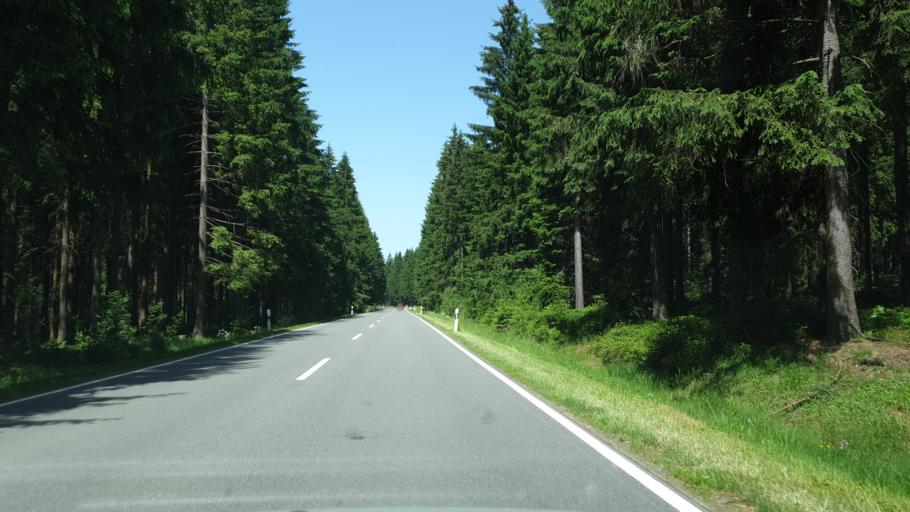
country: DE
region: Saxony
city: Hammerbrucke
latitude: 50.4040
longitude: 12.4224
